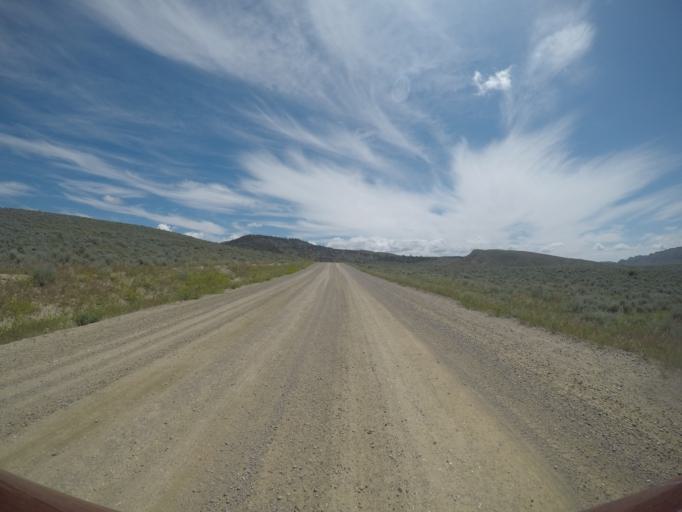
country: US
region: Montana
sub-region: Carbon County
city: Red Lodge
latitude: 45.2029
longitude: -108.8210
